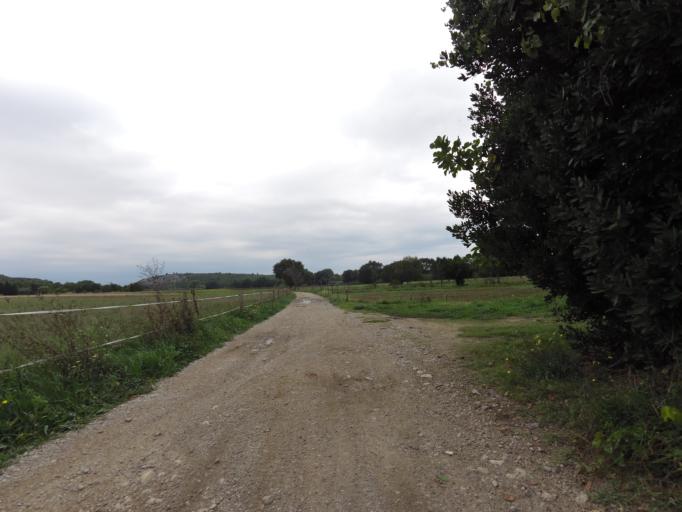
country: FR
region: Languedoc-Roussillon
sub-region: Departement de l'Herault
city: Villetelle
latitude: 43.7375
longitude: 4.1383
